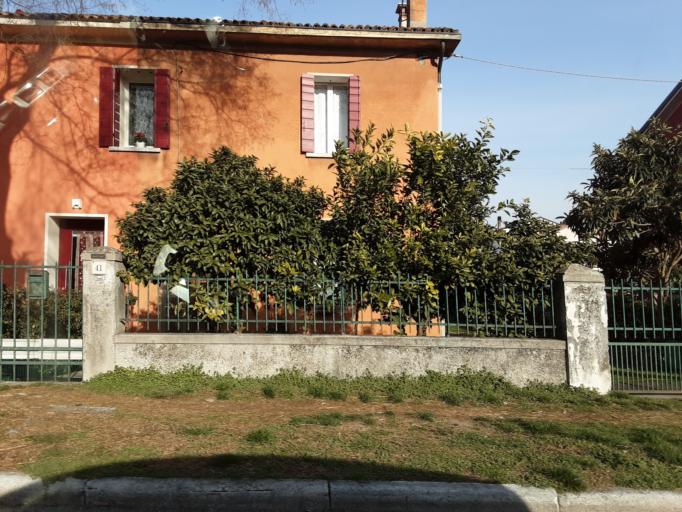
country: IT
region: Veneto
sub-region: Provincia di Treviso
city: Vittorio Veneto
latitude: 45.9841
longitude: 12.2998
